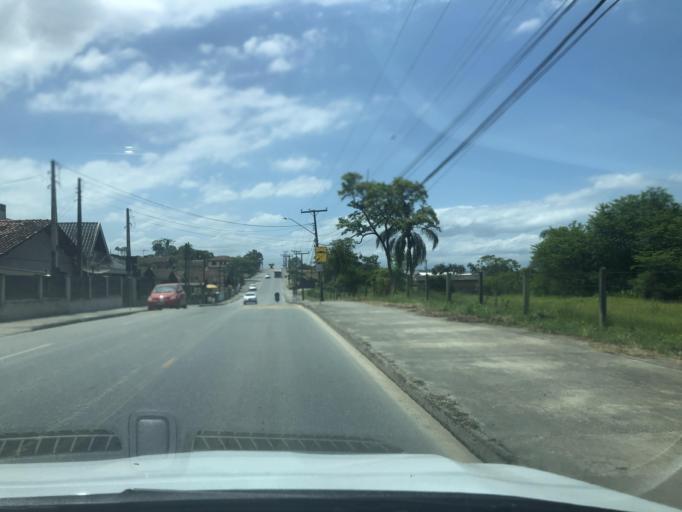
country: BR
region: Santa Catarina
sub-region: Joinville
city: Joinville
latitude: -26.3507
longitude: -48.7875
